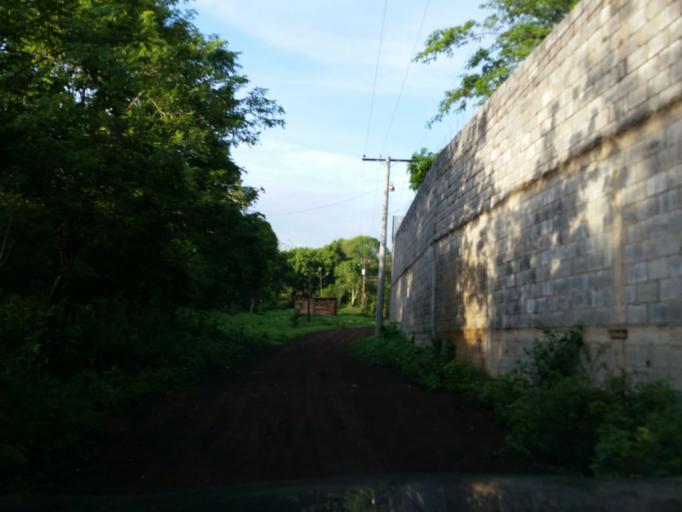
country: NI
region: Managua
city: Managua
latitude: 12.0902
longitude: -86.2367
